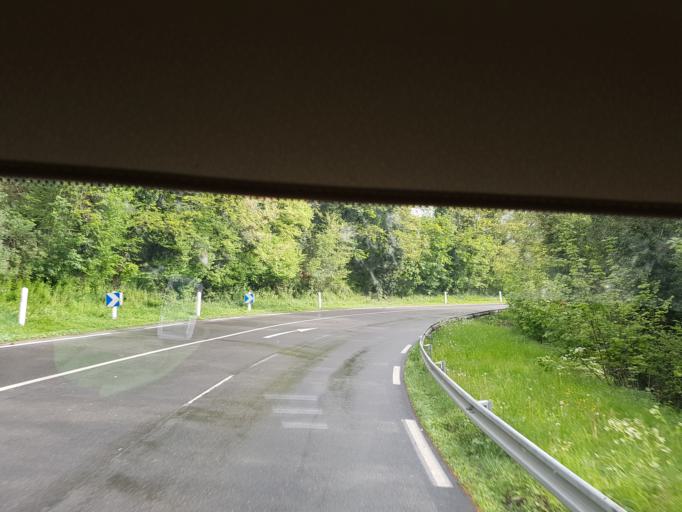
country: FR
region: Picardie
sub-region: Departement de l'Aisne
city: Cuffies
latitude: 49.4070
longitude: 3.3354
